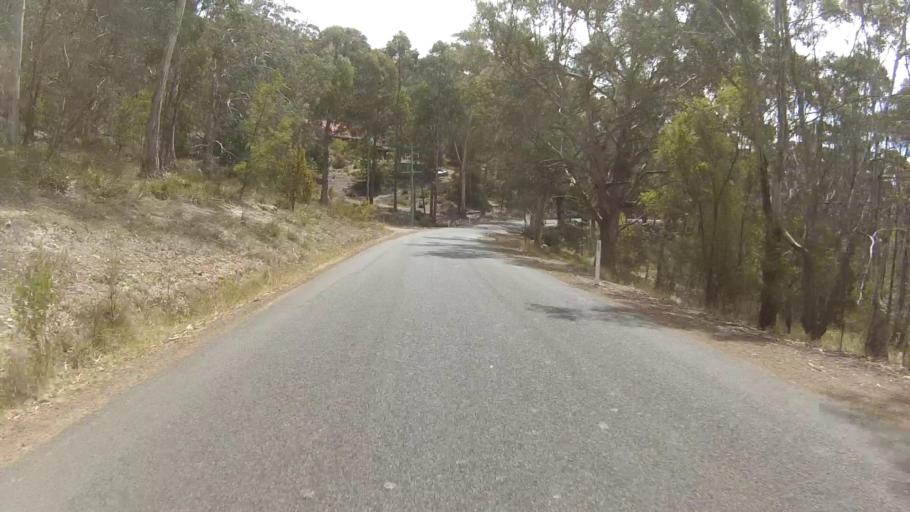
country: AU
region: Tasmania
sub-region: Kingborough
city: Blackmans Bay
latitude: -43.0499
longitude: 147.3396
